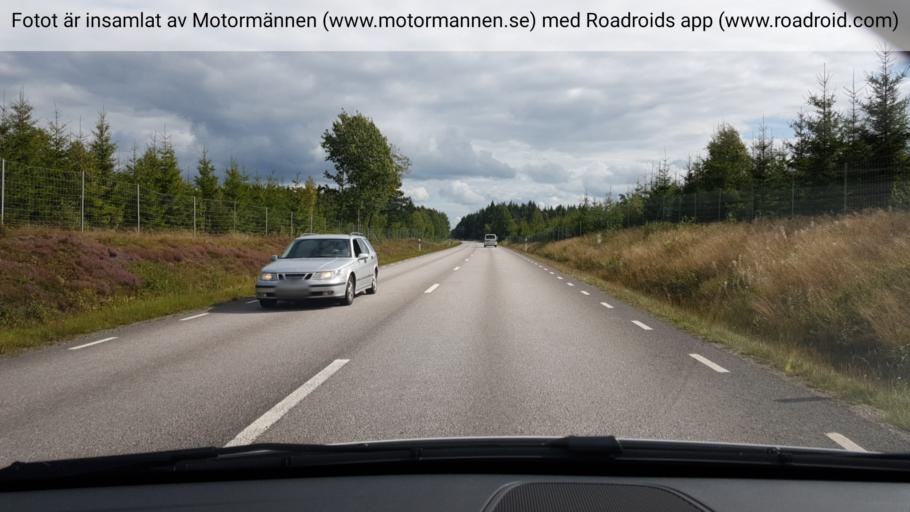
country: SE
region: Vaestra Goetaland
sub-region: Falkopings Kommun
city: Floby
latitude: 58.1952
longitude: 13.3287
